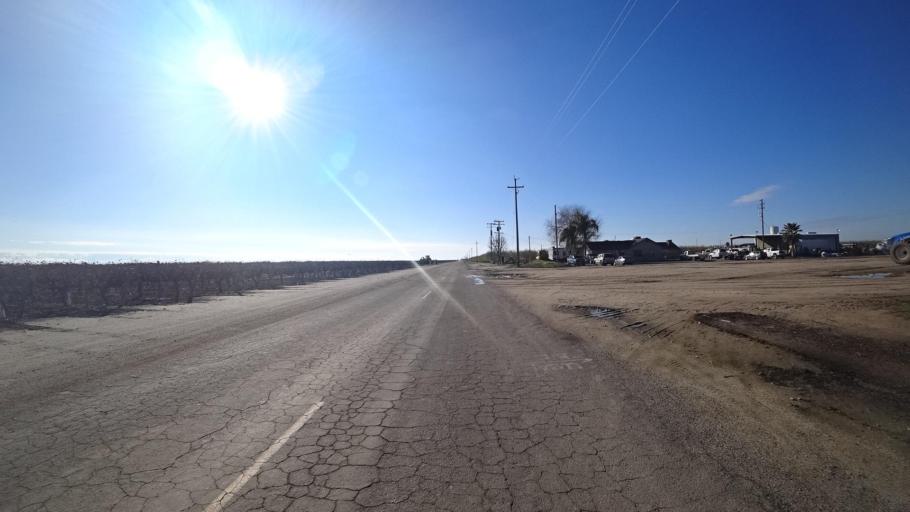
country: US
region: California
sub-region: Kern County
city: Delano
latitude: 35.7263
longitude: -119.2764
